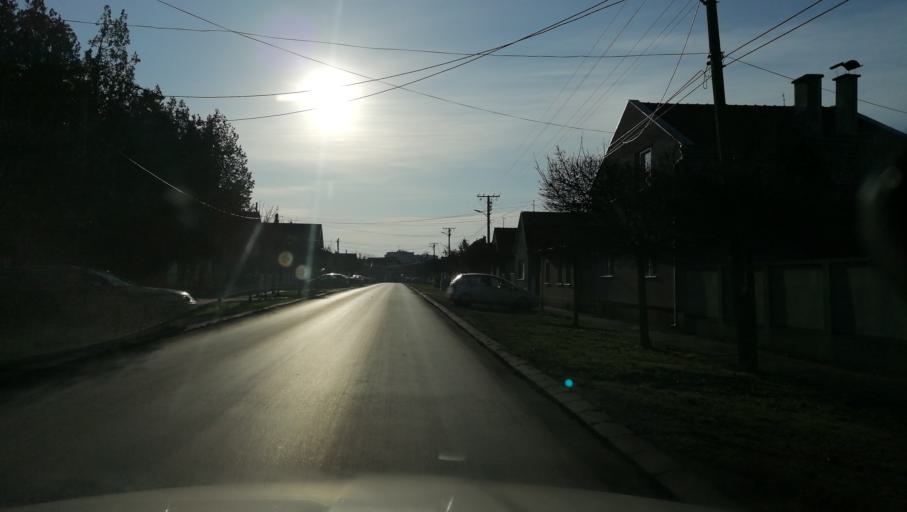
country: RS
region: Autonomna Pokrajina Vojvodina
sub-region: Sremski Okrug
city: Sremska Mitrovica
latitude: 44.9686
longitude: 19.6165
